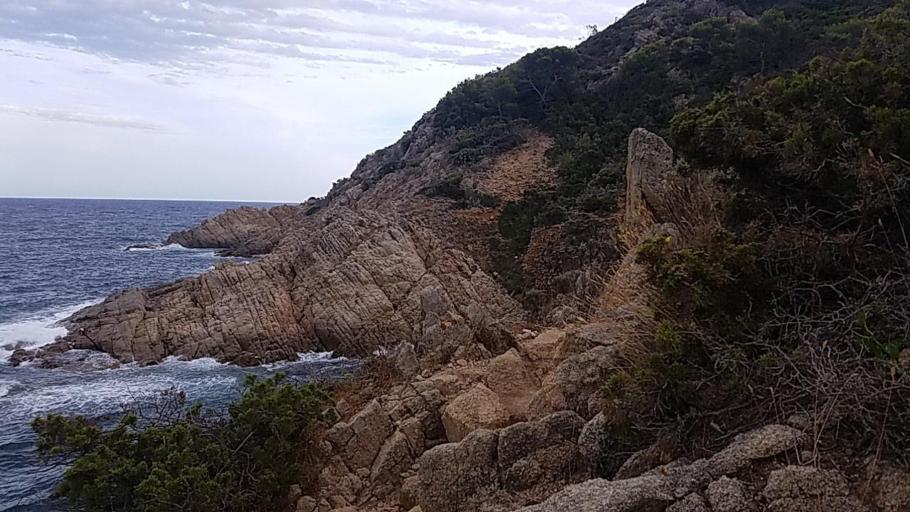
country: FR
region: Provence-Alpes-Cote d'Azur
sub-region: Departement du Var
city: Ramatuelle
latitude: 43.2052
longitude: 6.6720
